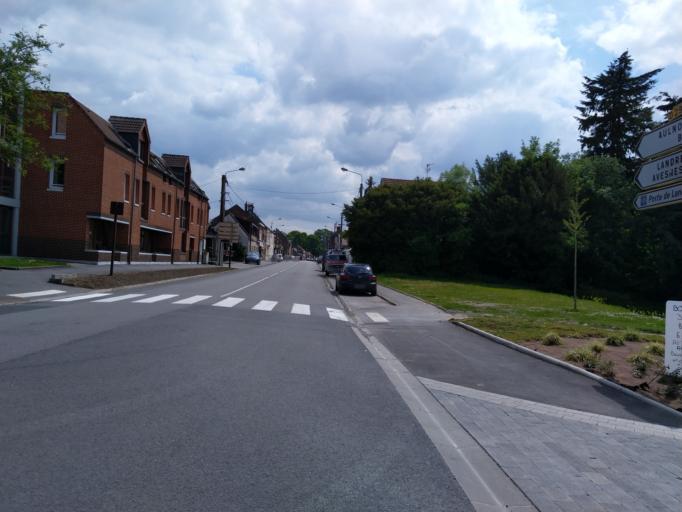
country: FR
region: Nord-Pas-de-Calais
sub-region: Departement du Nord
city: Le Quesnoy
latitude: 50.2456
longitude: 3.6423
